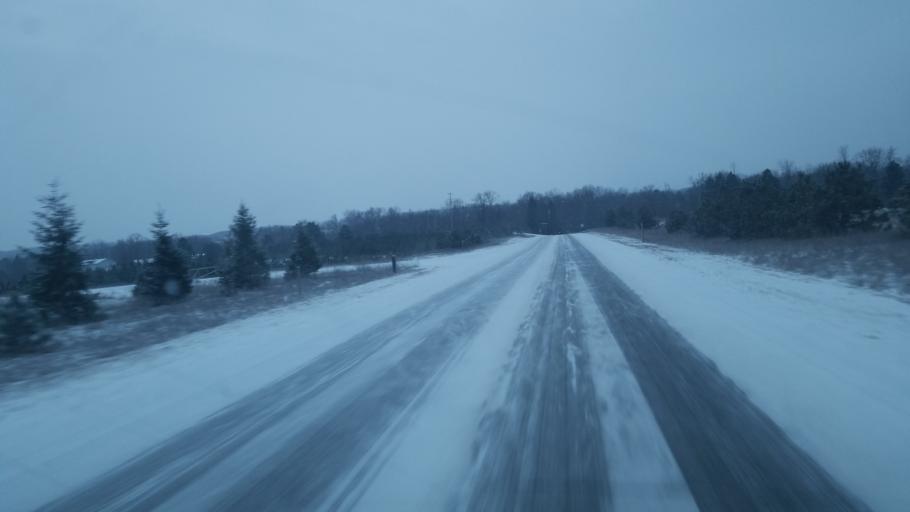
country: US
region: Michigan
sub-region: Osceola County
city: Reed City
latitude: 43.8480
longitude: -85.4285
